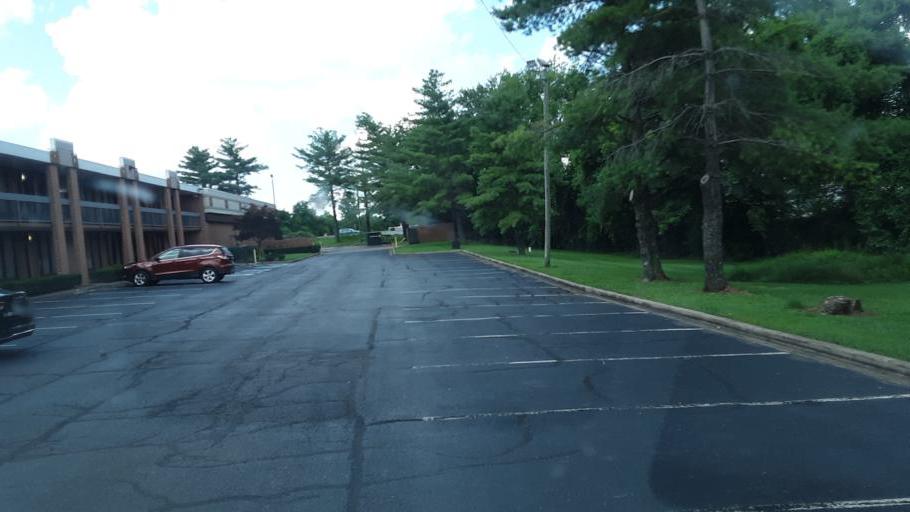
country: US
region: Tennessee
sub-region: Montgomery County
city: Clarksville
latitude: 36.5974
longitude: -87.2832
